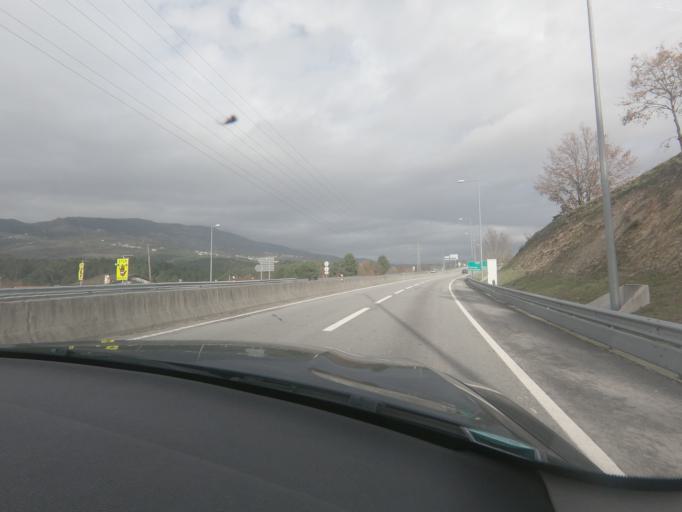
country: PT
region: Vila Real
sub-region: Vila Real
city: Vila Real
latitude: 41.3084
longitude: -7.7503
